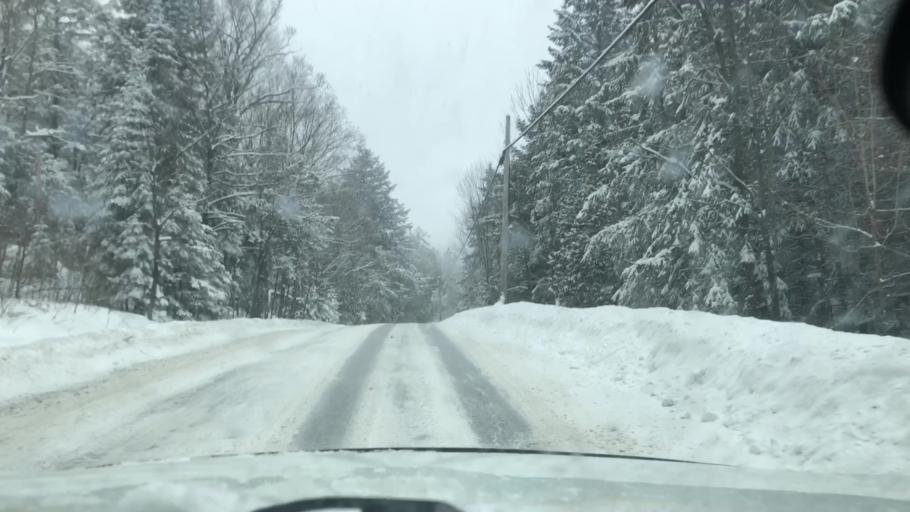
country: CA
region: Quebec
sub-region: Outaouais
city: Gatineau
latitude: 45.5167
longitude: -75.8441
